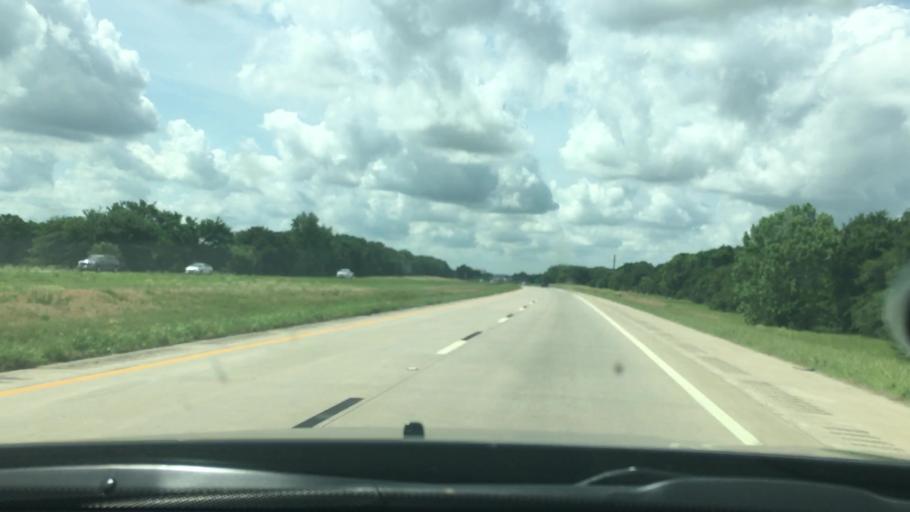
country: US
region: Oklahoma
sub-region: Love County
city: Marietta
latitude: 33.8069
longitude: -97.1349
